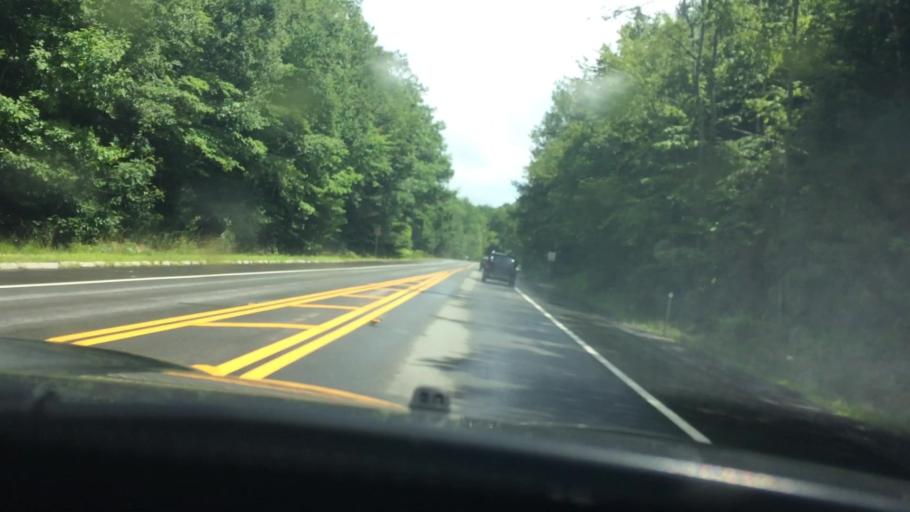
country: US
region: Massachusetts
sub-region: Worcester County
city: Phillipston
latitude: 42.5745
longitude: -72.1671
